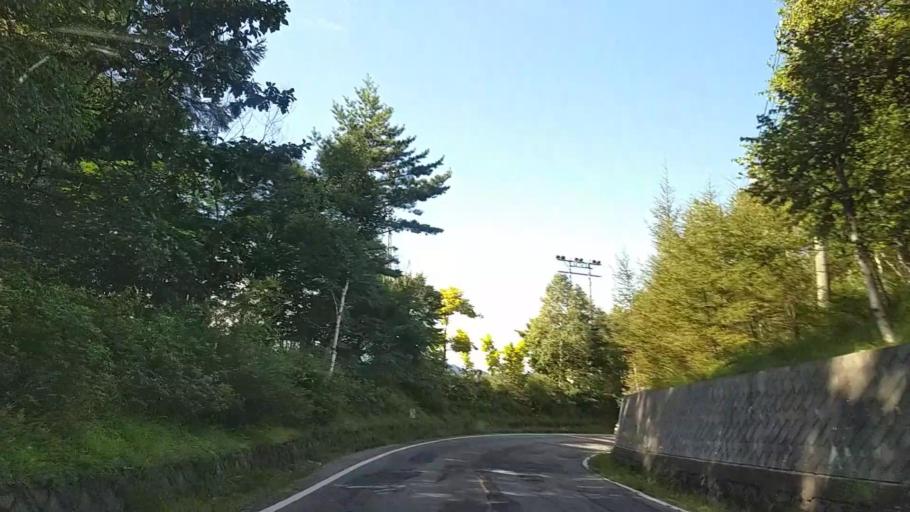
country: JP
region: Nagano
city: Chino
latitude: 36.1069
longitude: 138.2455
